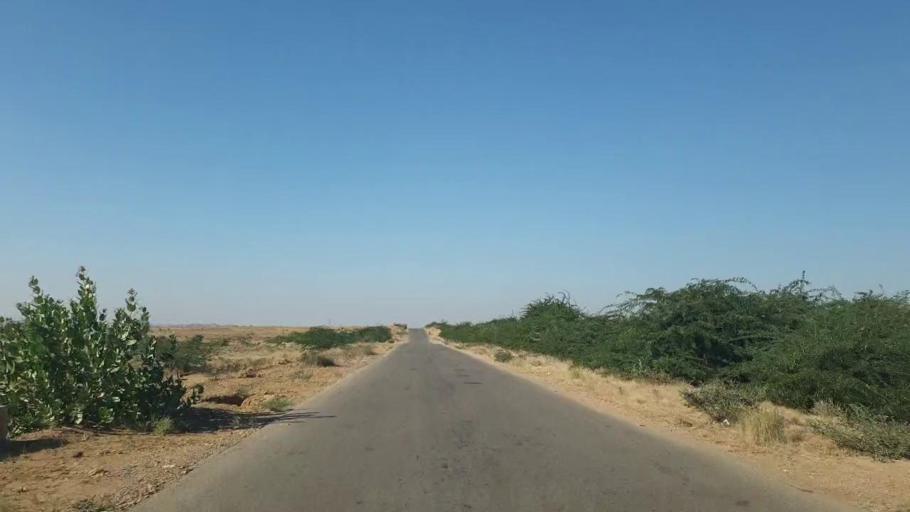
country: PK
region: Sindh
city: Malir Cantonment
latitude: 25.2638
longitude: 67.5976
